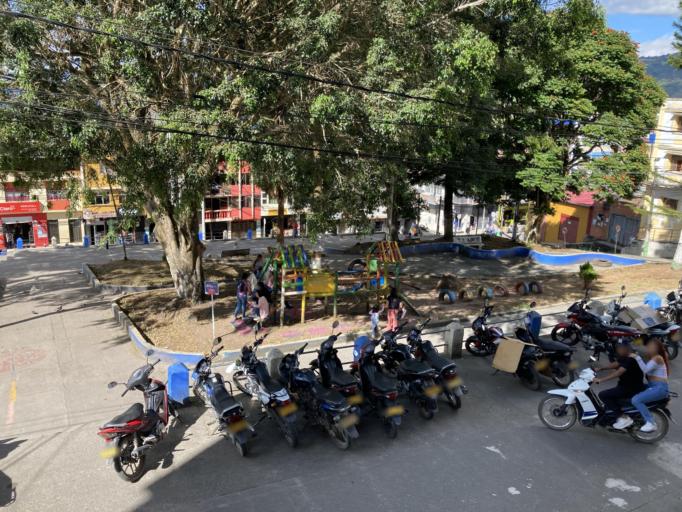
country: CO
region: Narino
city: La Union
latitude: 1.5994
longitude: -77.1322
